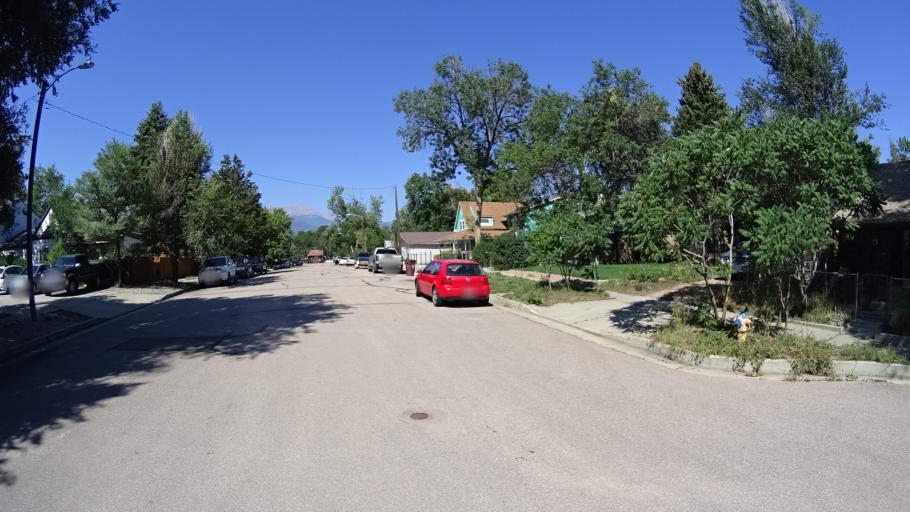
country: US
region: Colorado
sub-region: El Paso County
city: Colorado Springs
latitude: 38.8432
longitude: -104.8130
